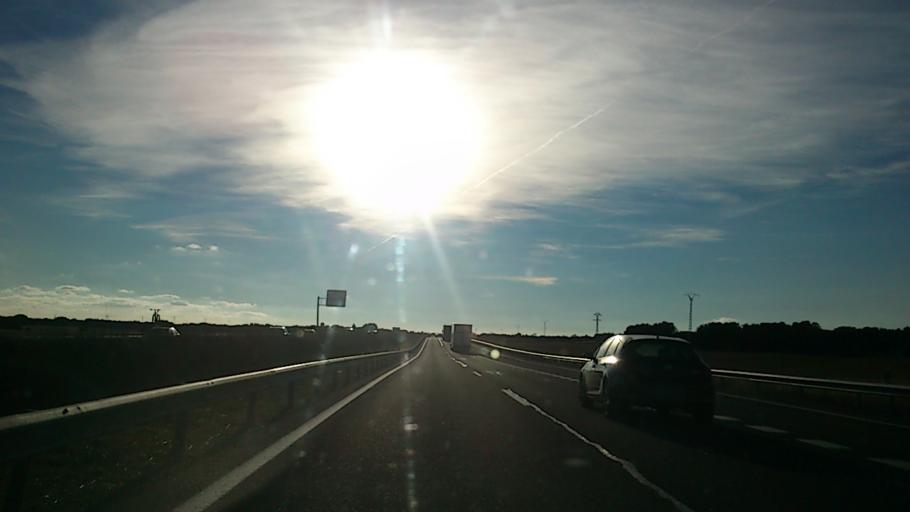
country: ES
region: Castille-La Mancha
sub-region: Provincia de Guadalajara
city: Mirabueno
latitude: 40.9278
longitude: -2.7173
